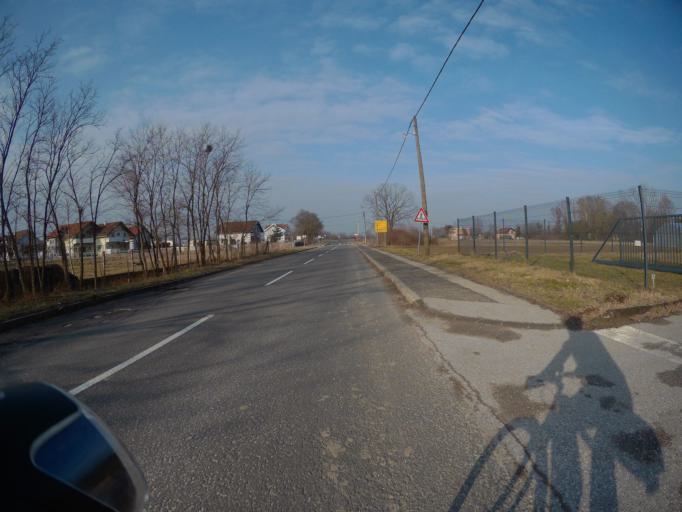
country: HR
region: Zagrebacka
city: Micevec
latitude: 45.7638
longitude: 16.0795
